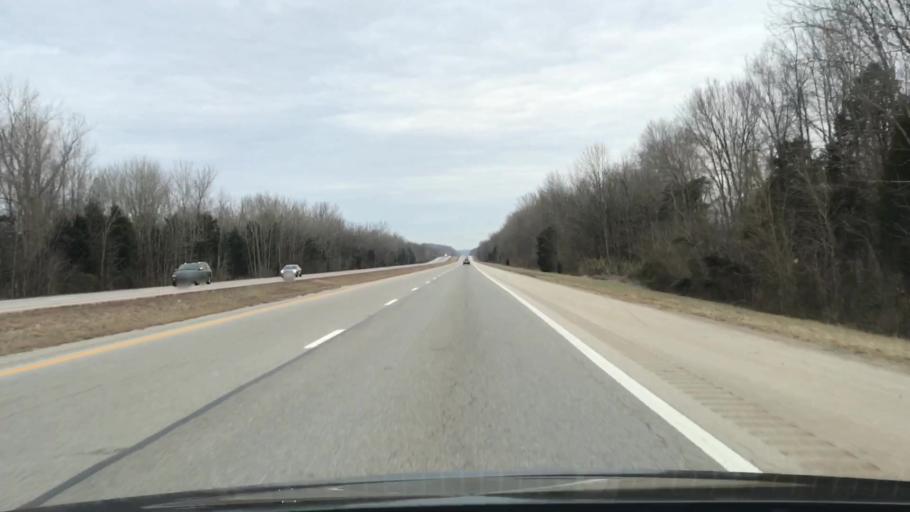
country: US
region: Kentucky
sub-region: Butler County
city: Morgantown
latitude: 37.1277
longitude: -86.6453
